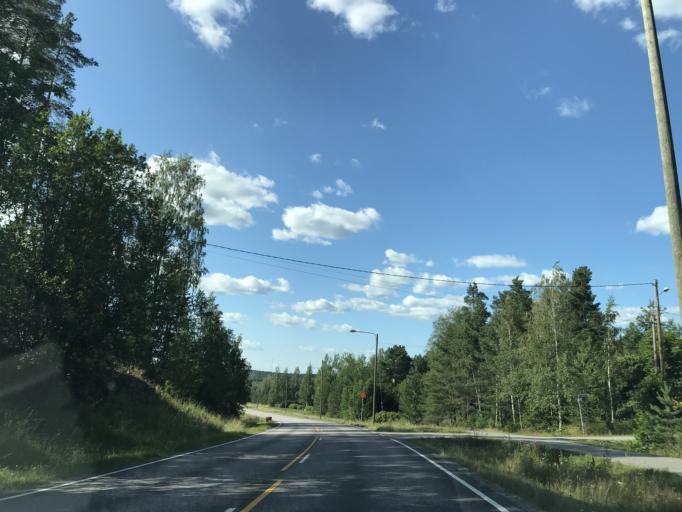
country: FI
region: Uusimaa
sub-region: Helsinki
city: Nurmijaervi
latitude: 60.4265
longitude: 24.8596
